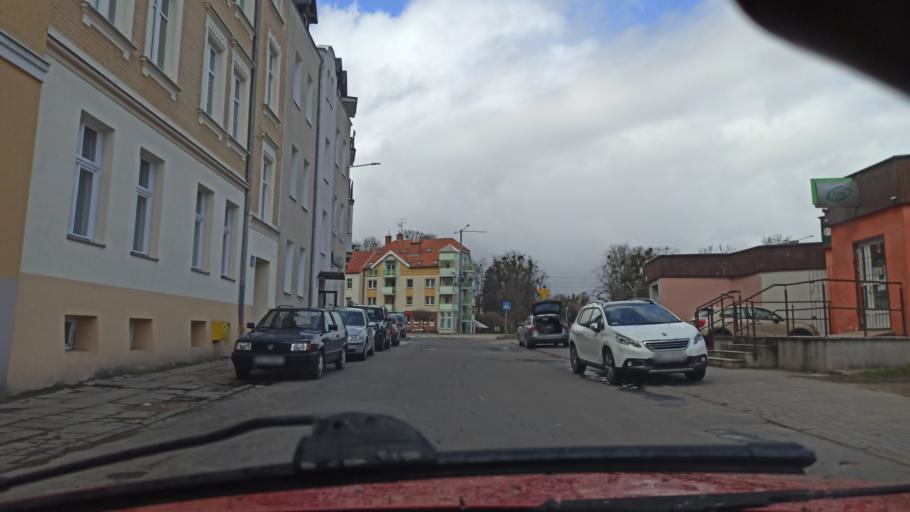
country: PL
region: Warmian-Masurian Voivodeship
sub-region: Powiat elblaski
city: Elblag
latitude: 54.1583
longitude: 19.4134
